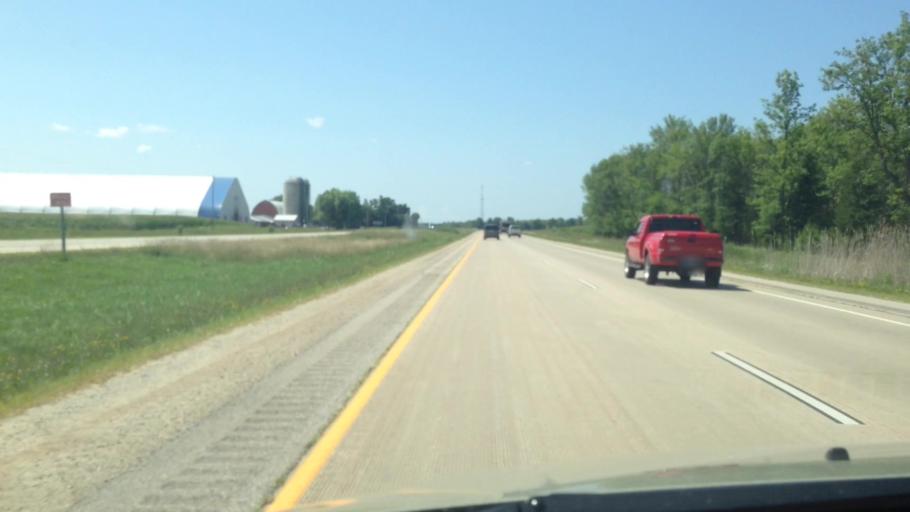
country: US
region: Wisconsin
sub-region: Marinette County
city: Peshtigo
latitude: 45.0123
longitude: -87.8430
